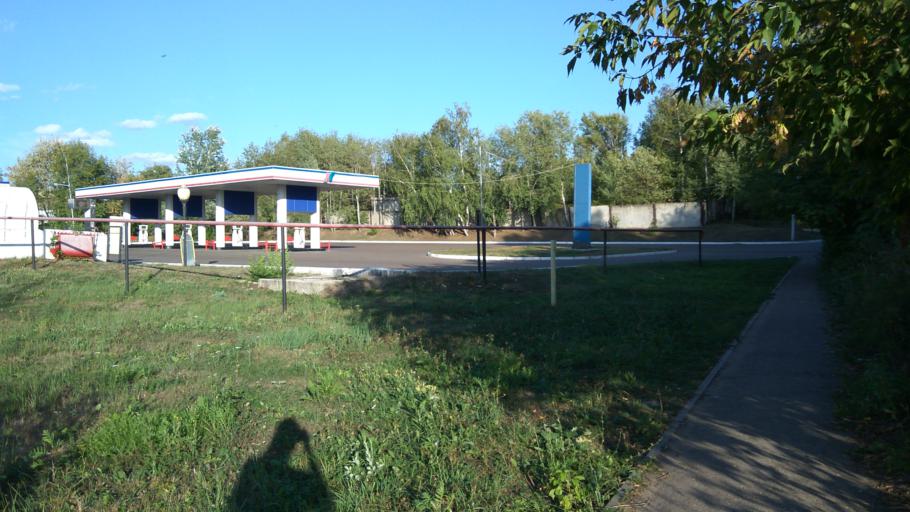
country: RU
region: Tatarstan
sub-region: Gorod Kazan'
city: Kazan
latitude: 55.7358
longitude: 49.0963
